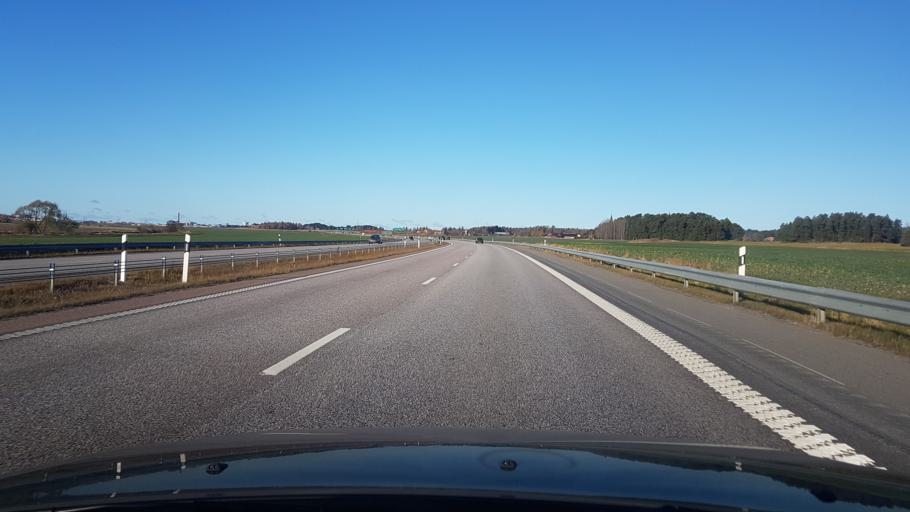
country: SE
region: Uppsala
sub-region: Uppsala Kommun
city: Saevja
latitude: 59.8196
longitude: 17.7524
